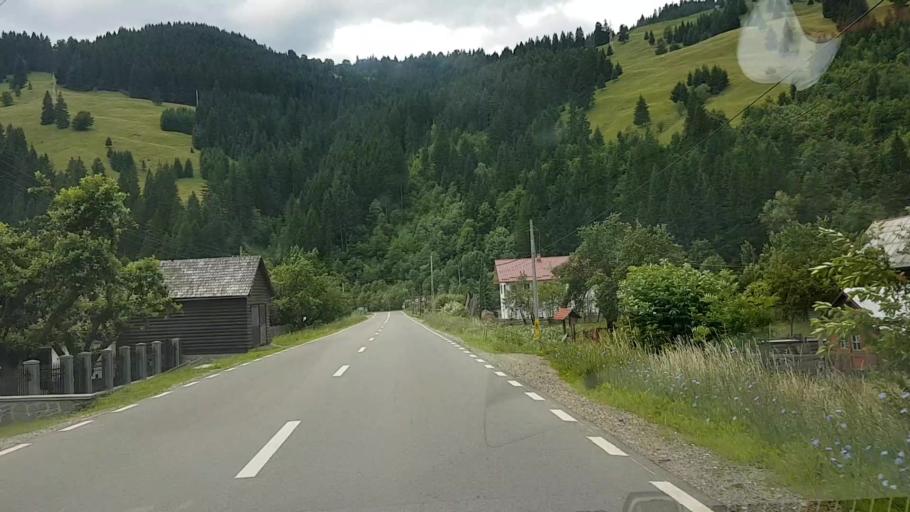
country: RO
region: Neamt
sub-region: Comuna Farcasa
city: Farcasa
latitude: 47.1426
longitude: 25.8611
